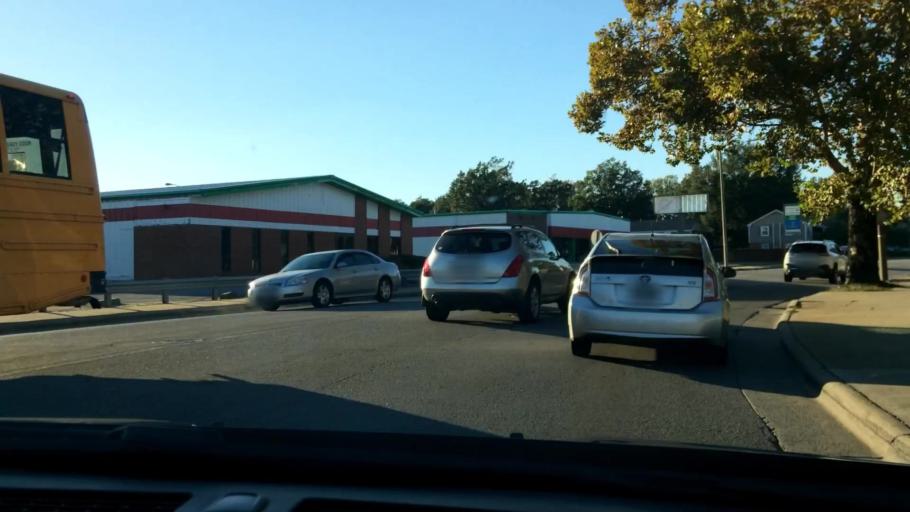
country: US
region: North Carolina
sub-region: Pitt County
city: Greenville
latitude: 35.6028
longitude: -77.3811
